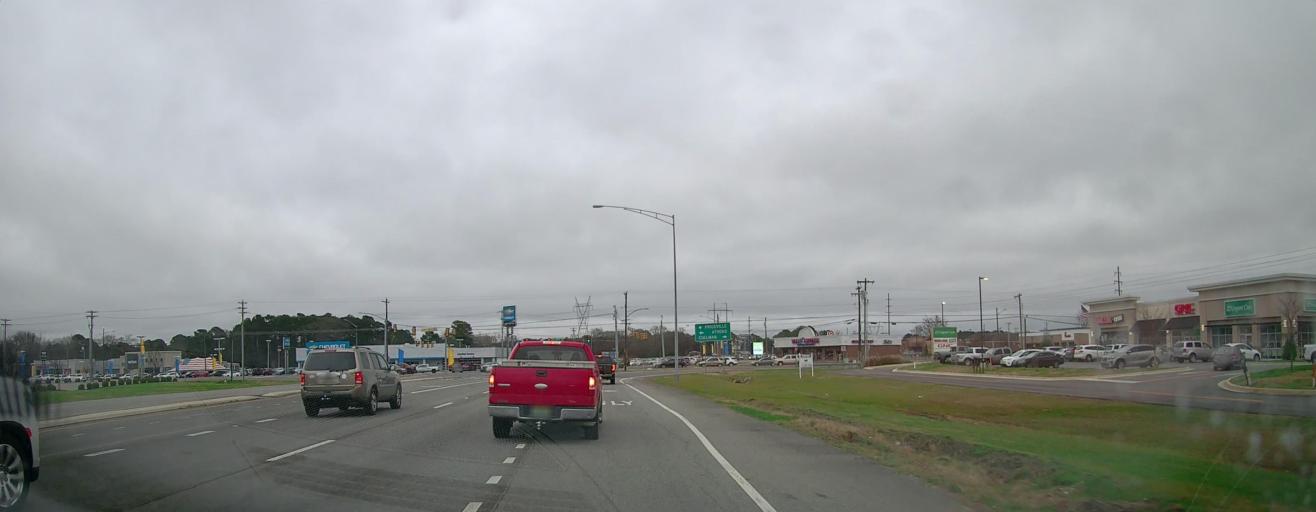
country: US
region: Alabama
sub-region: Morgan County
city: Flint City
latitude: 34.5623
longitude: -86.9748
